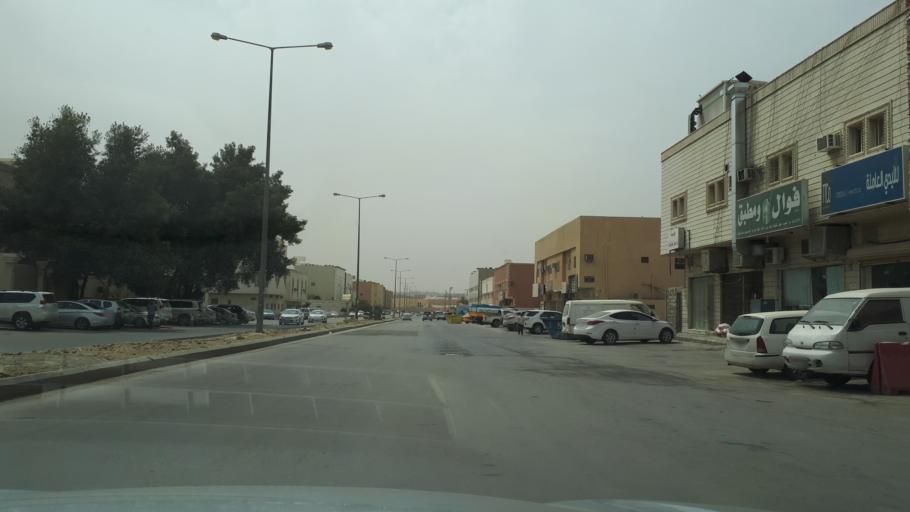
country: SA
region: Ar Riyad
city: Riyadh
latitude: 24.7514
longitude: 46.6397
